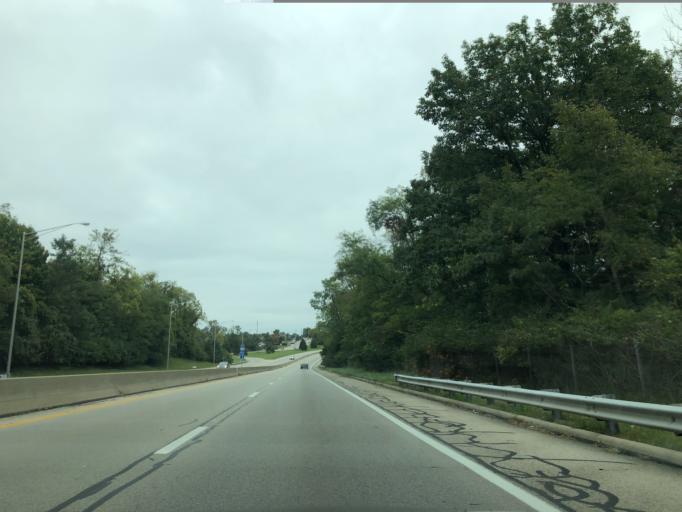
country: US
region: Ohio
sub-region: Hamilton County
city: Dillonvale
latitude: 39.2237
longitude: -84.4031
